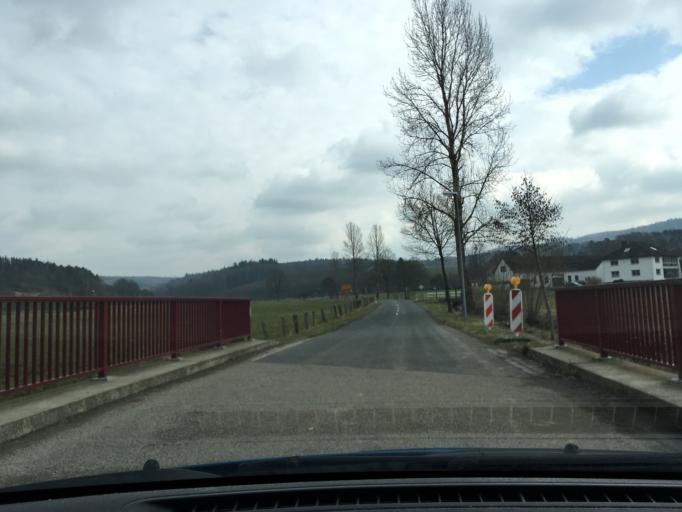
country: DE
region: Lower Saxony
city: Adelebsen
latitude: 51.5915
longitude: 9.6781
